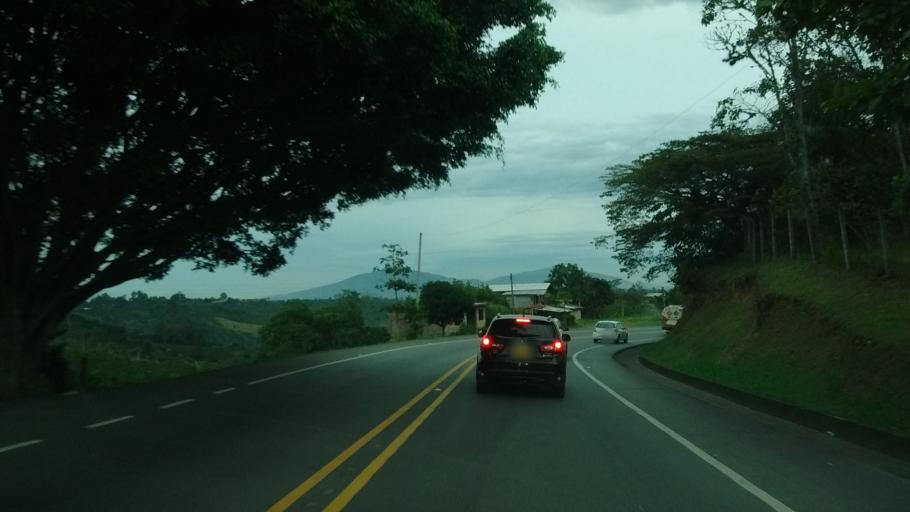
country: CO
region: Cauca
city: Morales
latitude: 2.7743
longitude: -76.5547
